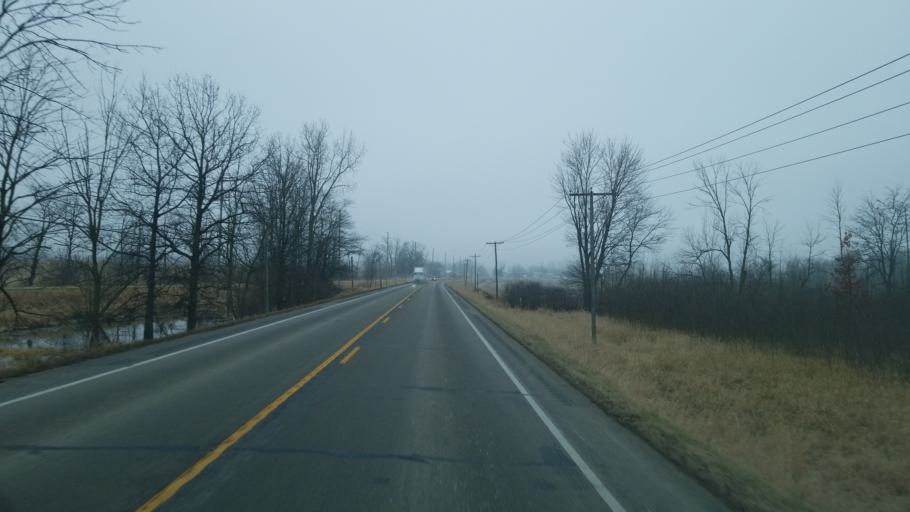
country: US
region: Indiana
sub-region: Adams County
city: Geneva
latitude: 40.5784
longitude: -84.9586
